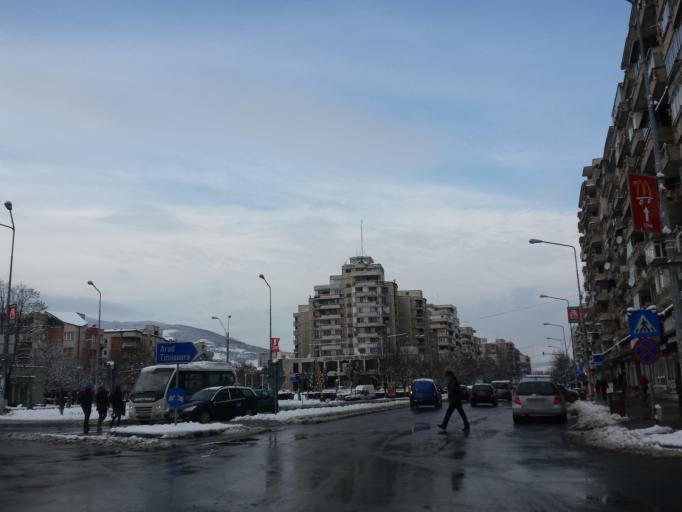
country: RO
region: Hunedoara
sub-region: Municipiul Deva
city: Deva
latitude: 45.8739
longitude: 22.9089
